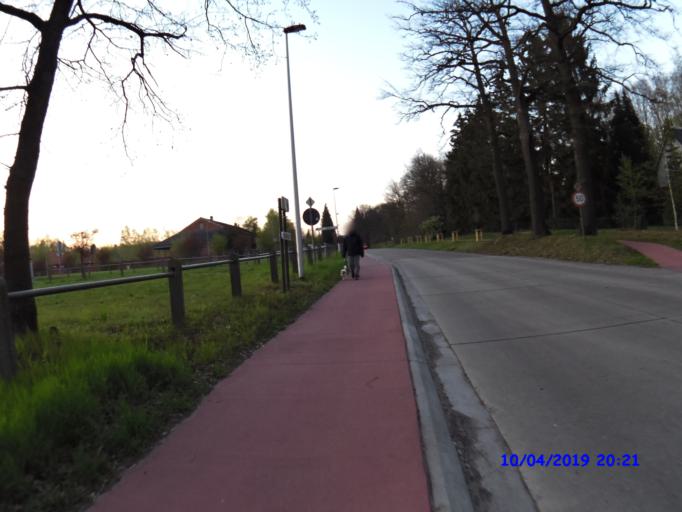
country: BE
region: Flanders
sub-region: Provincie Limburg
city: Leopoldsburg
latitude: 51.1091
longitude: 5.2645
